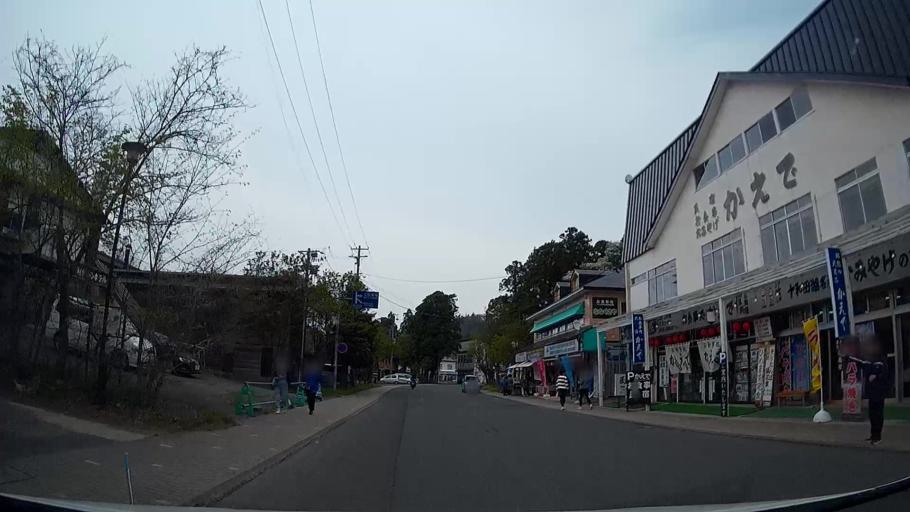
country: JP
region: Akita
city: Hanawa
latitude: 40.4274
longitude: 140.8940
